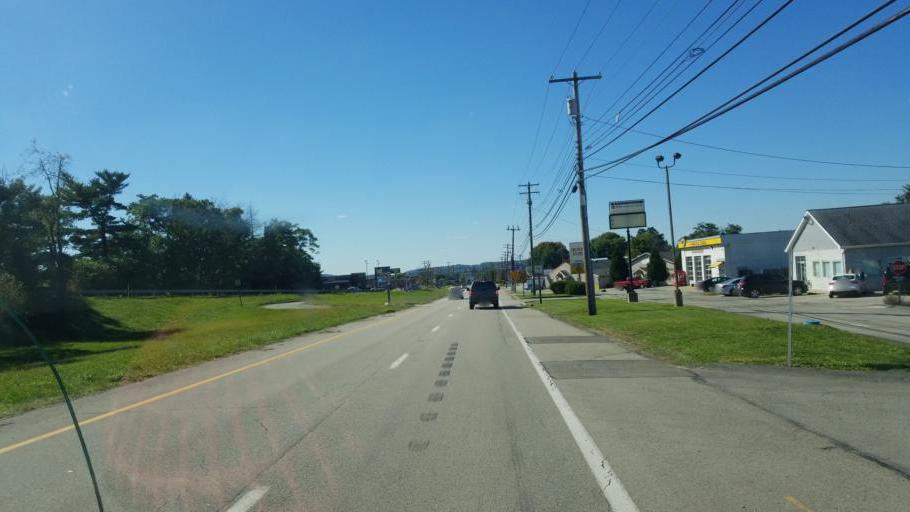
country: US
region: Pennsylvania
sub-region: Westmoreland County
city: Greensburg
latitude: 40.3025
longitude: -79.5196
